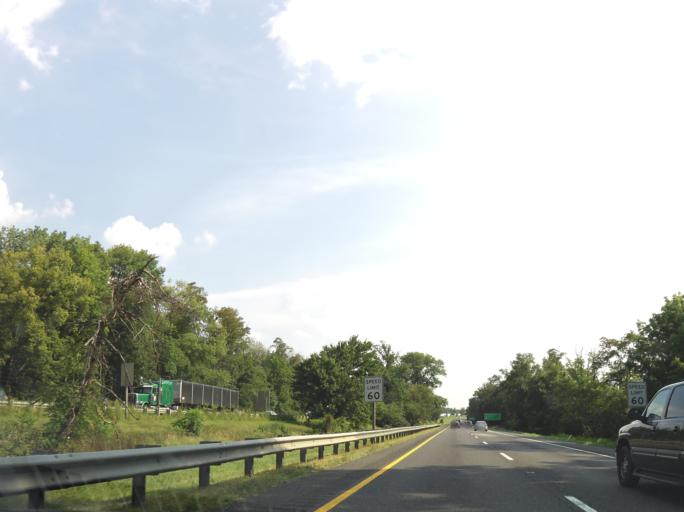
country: US
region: Maryland
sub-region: Washington County
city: Fountainhead-Orchard Hills
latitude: 39.6784
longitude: -77.7342
